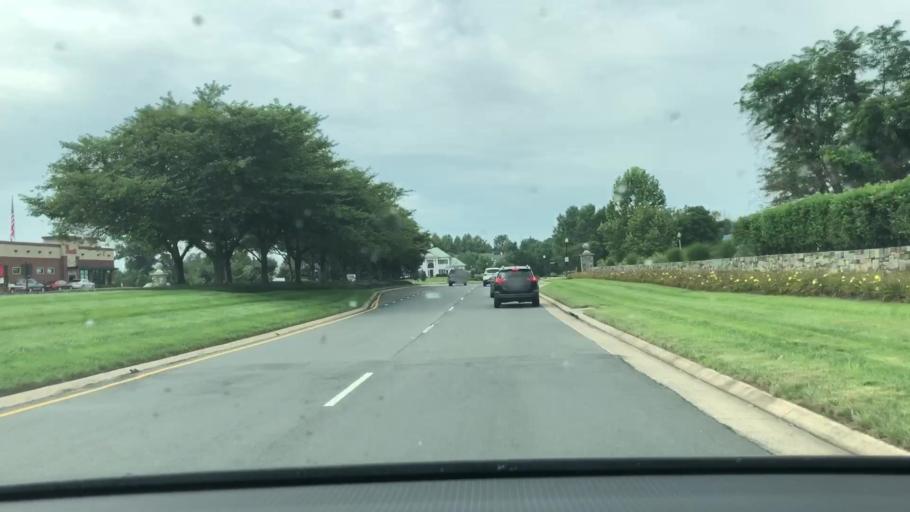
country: US
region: Virginia
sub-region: Loudoun County
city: South Riding
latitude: 38.9231
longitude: -77.5050
